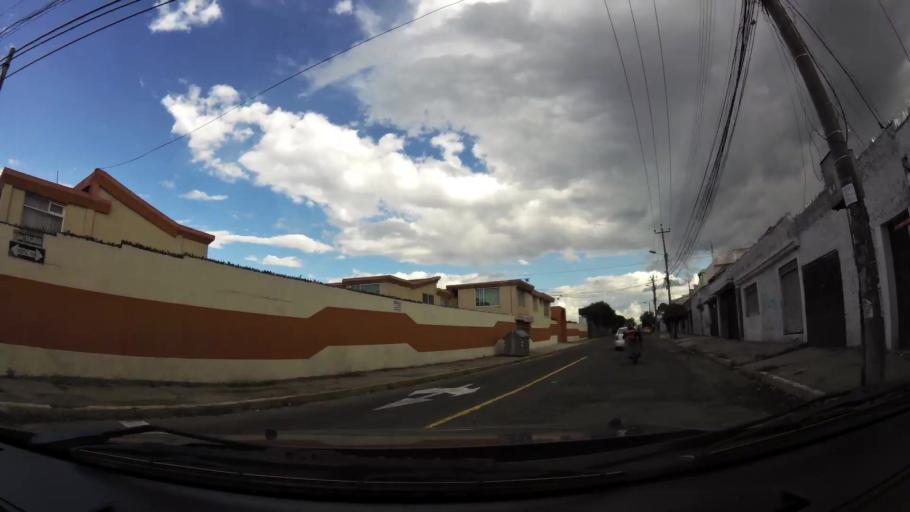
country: EC
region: Pichincha
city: Quito
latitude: -0.1232
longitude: -78.4918
